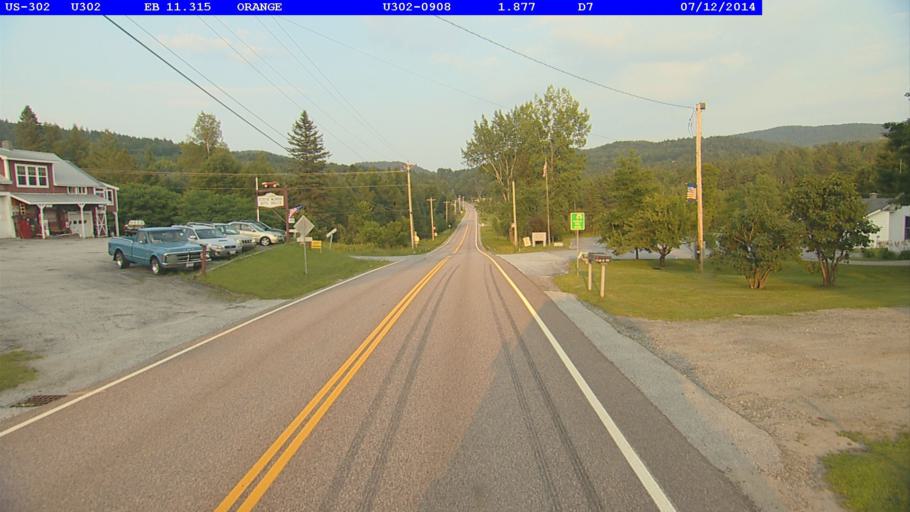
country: US
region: Vermont
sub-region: Washington County
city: South Barre
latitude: 44.1485
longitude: -72.4019
